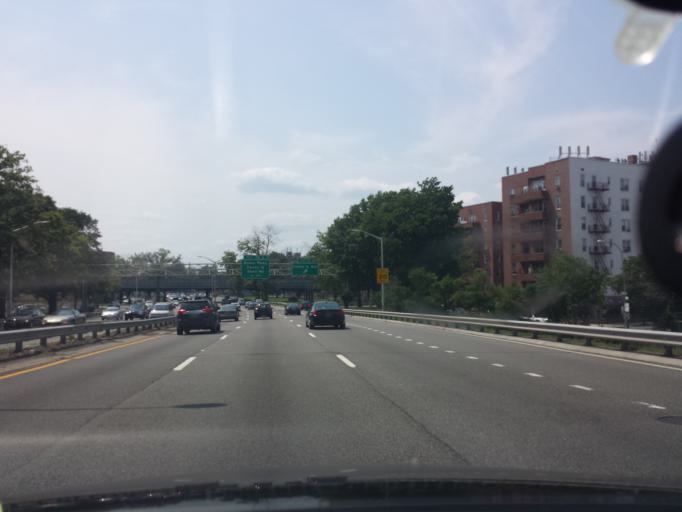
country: US
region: New York
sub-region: Kings County
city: Coney Island
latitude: 40.5848
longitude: -73.9523
